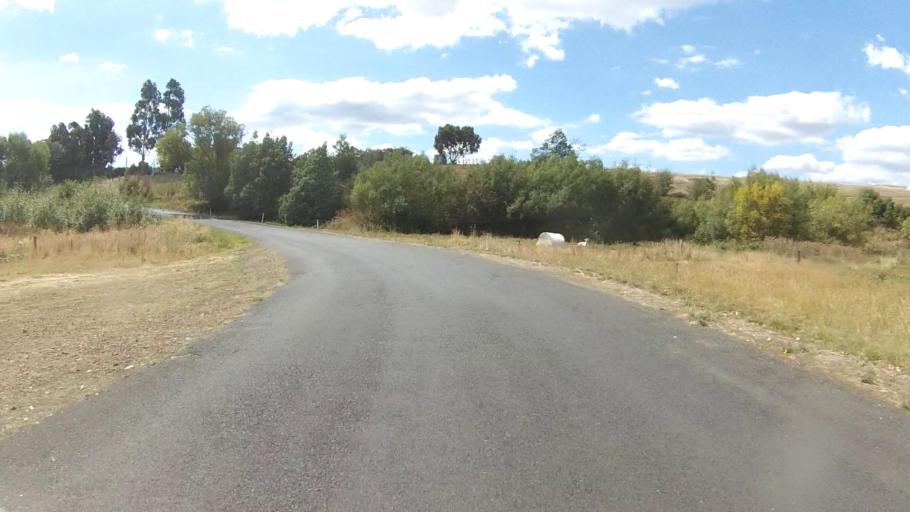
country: AU
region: Tasmania
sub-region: Derwent Valley
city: New Norfolk
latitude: -42.7529
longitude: 146.9713
